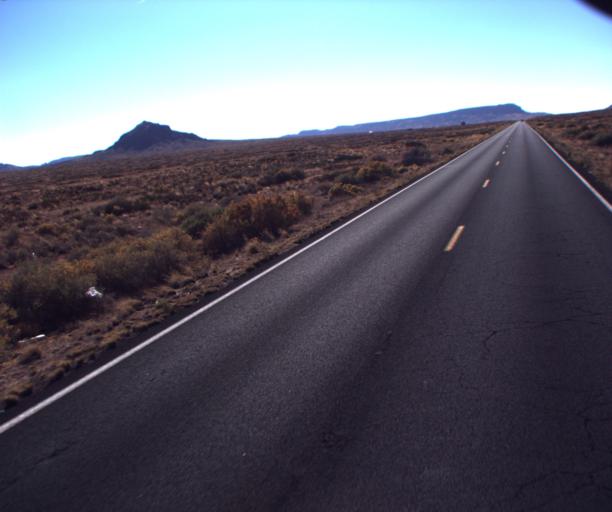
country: US
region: Arizona
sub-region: Navajo County
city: Dilkon
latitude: 35.4890
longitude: -110.4304
